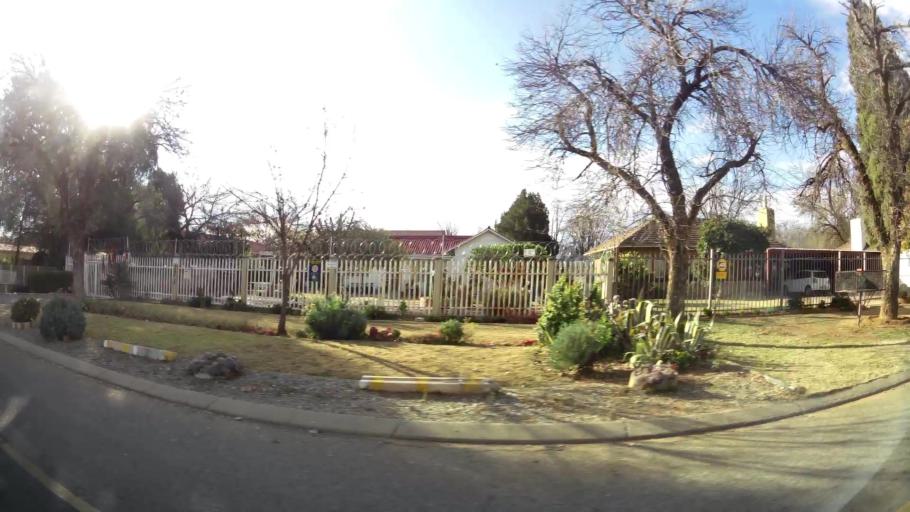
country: ZA
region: Orange Free State
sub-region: Lejweleputswa District Municipality
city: Welkom
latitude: -27.9819
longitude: 26.7147
